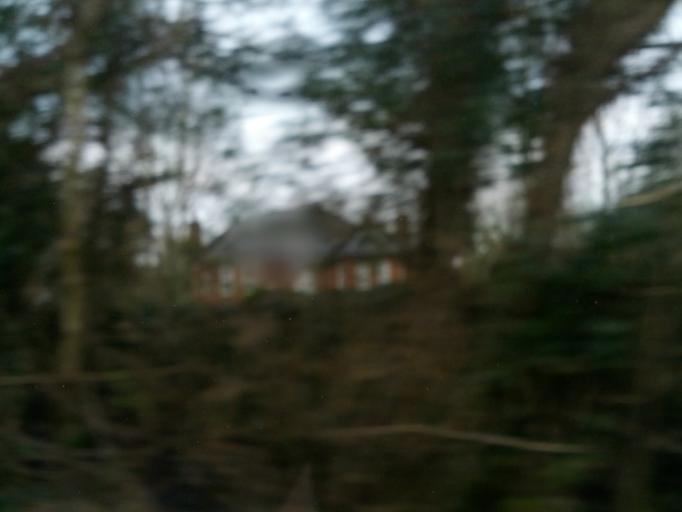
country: IE
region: Connaught
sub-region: County Galway
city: Oranmore
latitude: 53.2348
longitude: -8.8419
